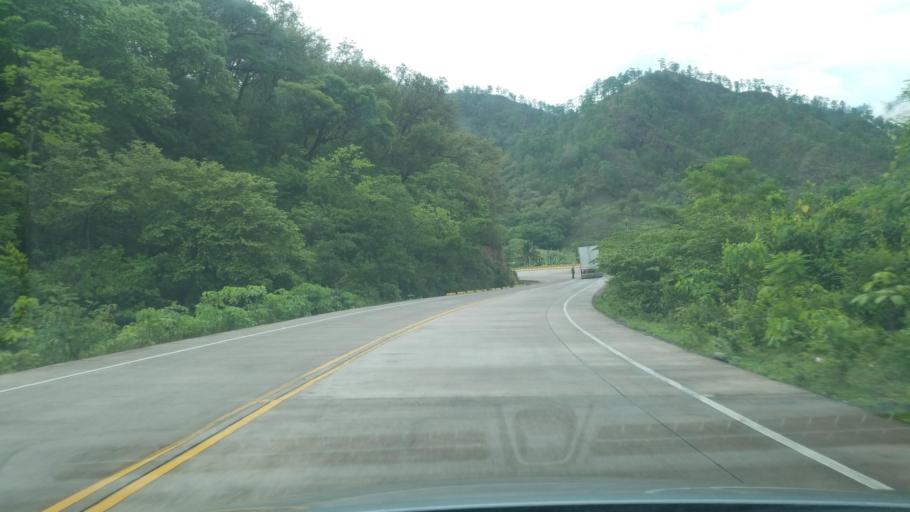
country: HN
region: Copan
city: Copan
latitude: 14.8551
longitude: -89.2179
